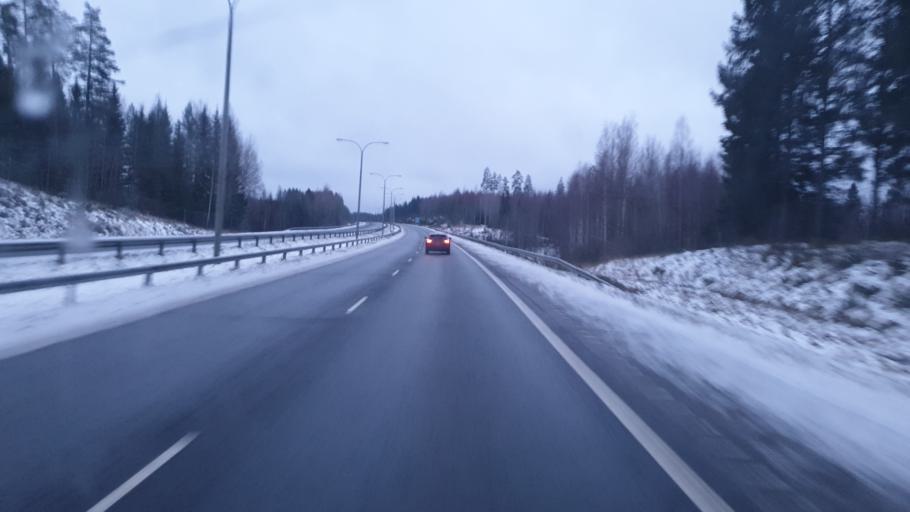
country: FI
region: Northern Savo
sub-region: Kuopio
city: Siilinjaervi
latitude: 63.0298
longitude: 27.6567
